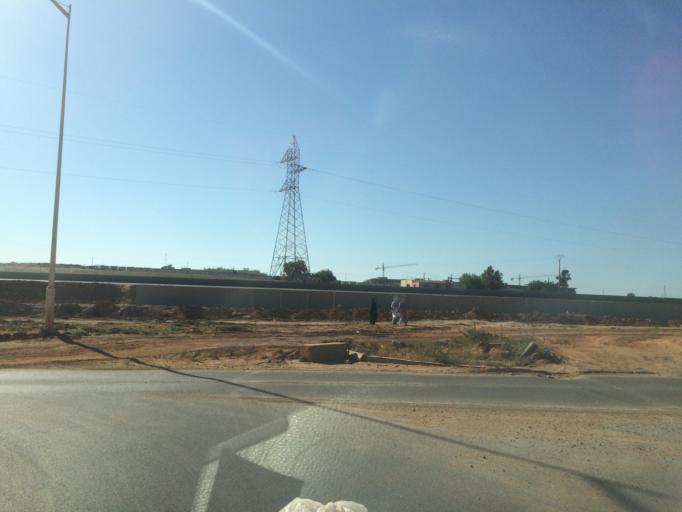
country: MA
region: Rabat-Sale-Zemmour-Zaer
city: Sale
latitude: 33.9881
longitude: -6.7275
